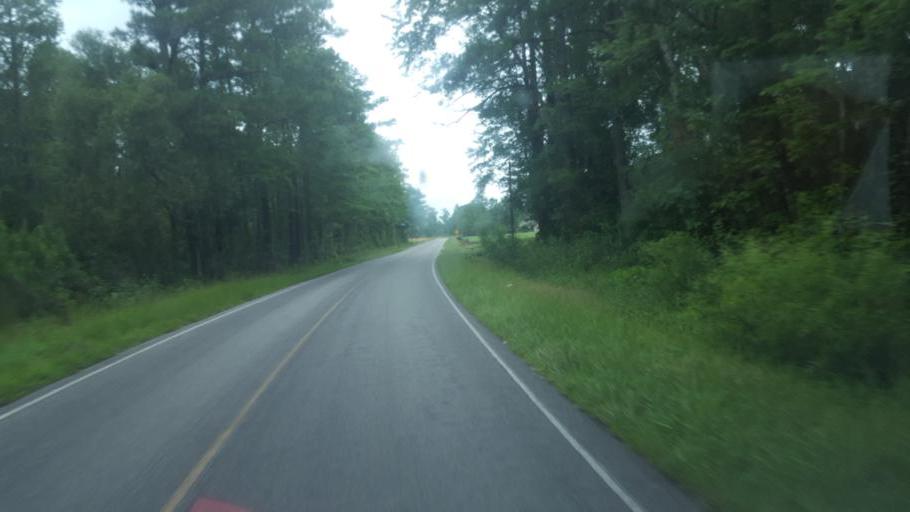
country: US
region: North Carolina
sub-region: Tyrrell County
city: Columbia
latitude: 35.9338
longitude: -76.2671
